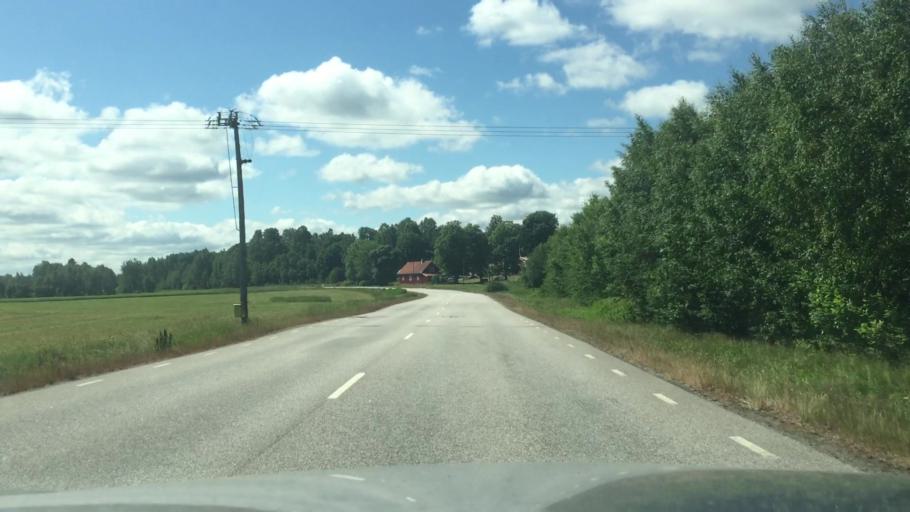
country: SE
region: Vaestra Goetaland
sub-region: Karlsborgs Kommun
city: Molltorp
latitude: 58.6321
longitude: 14.3901
